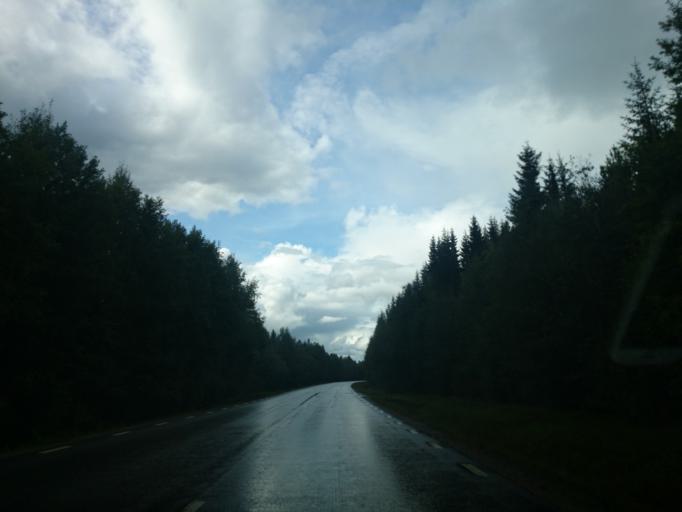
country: SE
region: Jaemtland
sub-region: Bergs Kommun
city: Hoverberg
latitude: 62.4917
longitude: 14.6092
